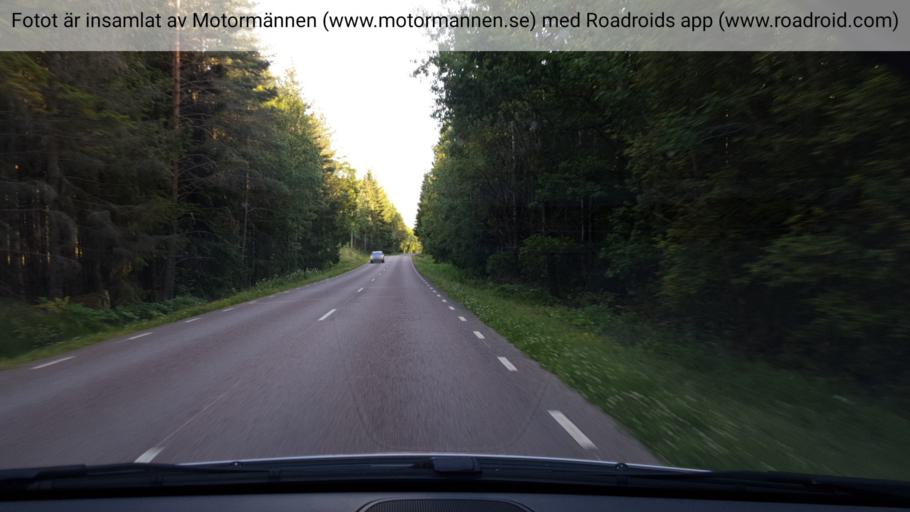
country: SE
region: Vaestmanland
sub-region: Vasteras
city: Tillberga
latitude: 59.7207
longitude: 16.6661
